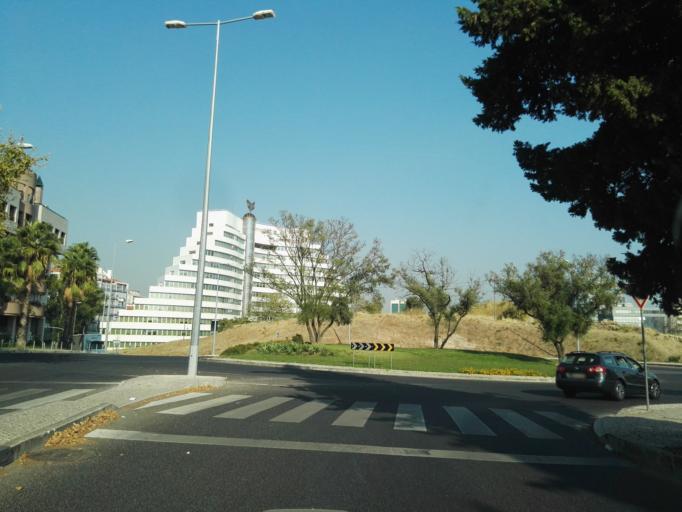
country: PT
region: Lisbon
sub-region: Lisbon
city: Lisbon
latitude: 38.7439
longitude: -9.1529
